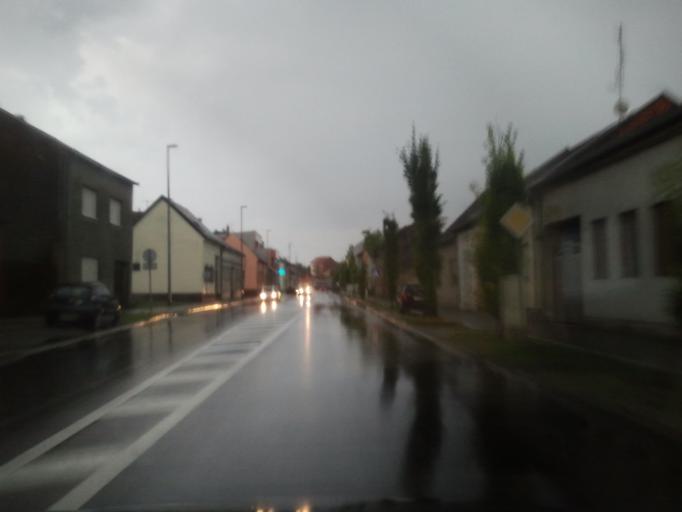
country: HR
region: Vukovarsko-Srijemska
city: Vukovar
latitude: 45.3468
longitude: 19.0066
